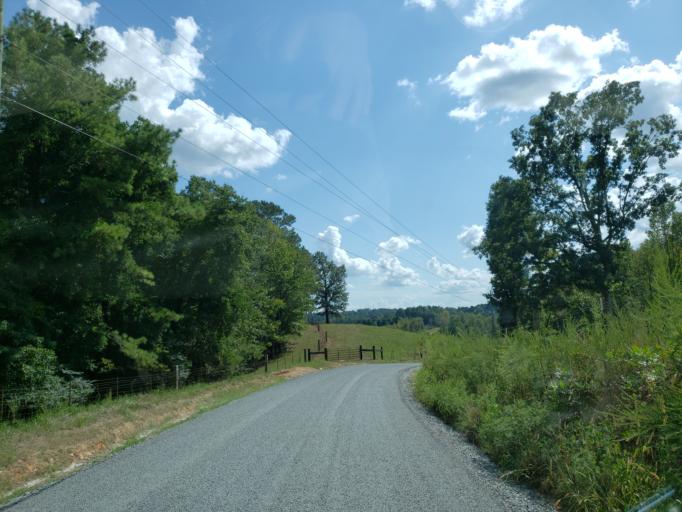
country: US
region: Georgia
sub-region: Pickens County
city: Jasper
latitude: 34.4243
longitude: -84.4559
